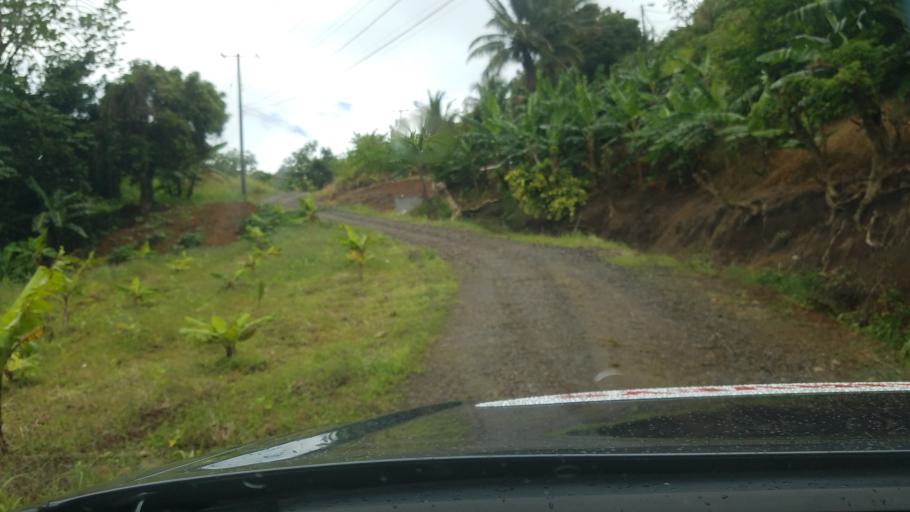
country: LC
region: Castries Quarter
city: Bisee
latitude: 13.9997
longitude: -60.9573
